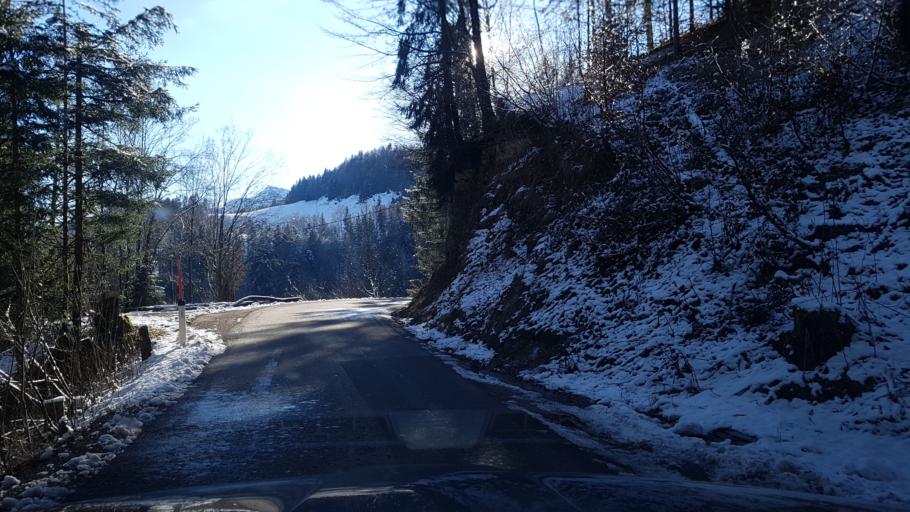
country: AT
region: Salzburg
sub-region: Politischer Bezirk Salzburg-Umgebung
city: Faistenau
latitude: 47.7764
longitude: 13.2133
